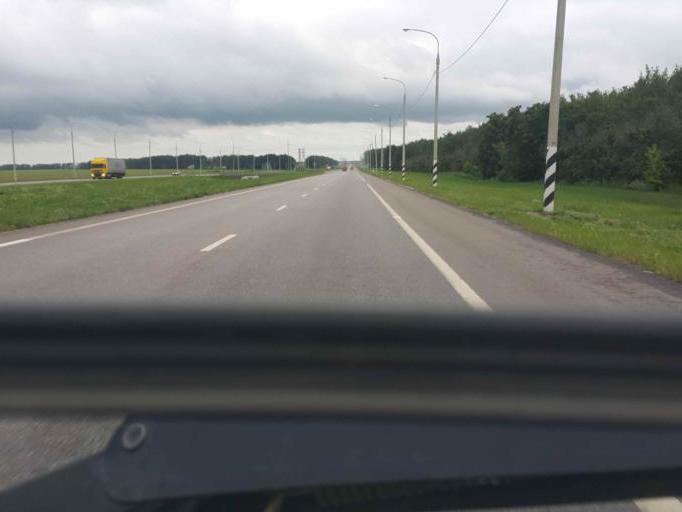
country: RU
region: Tambov
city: Zavoronezhskoye
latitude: 52.8456
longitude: 40.8222
